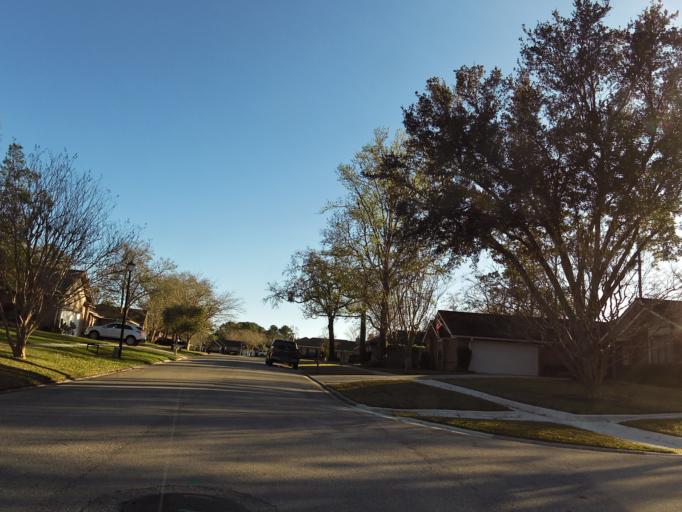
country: US
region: Florida
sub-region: Saint Johns County
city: Fruit Cove
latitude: 30.2129
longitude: -81.6065
